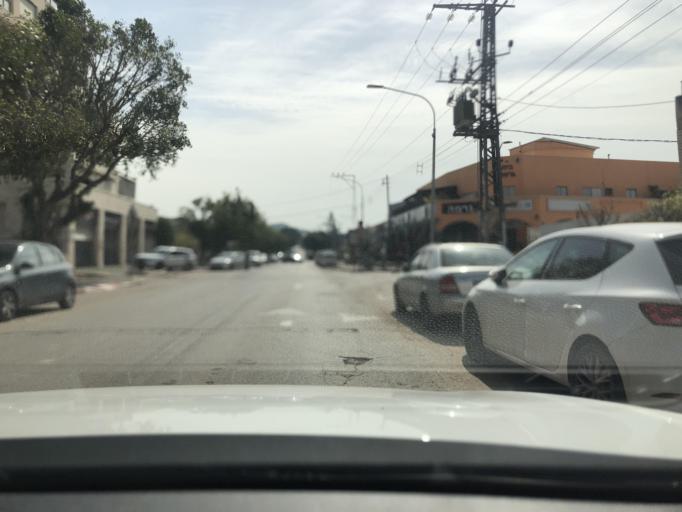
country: IL
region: Central District
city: Rosh Ha'Ayin
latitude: 32.0939
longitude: 34.9457
